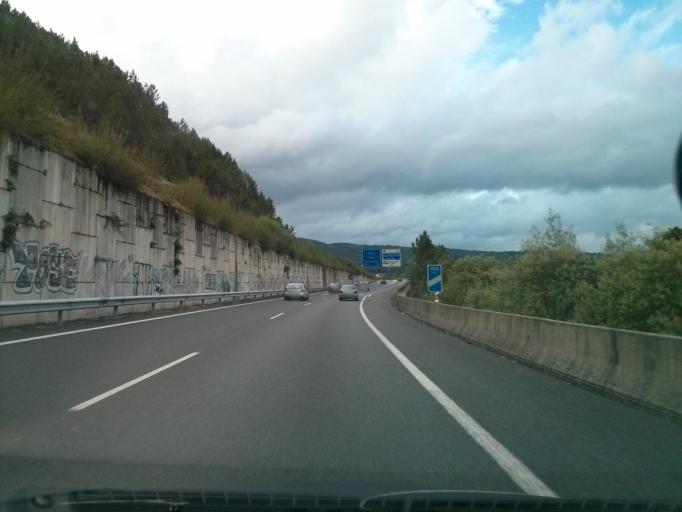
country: ES
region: Galicia
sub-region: Provincia de Ourense
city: Toen
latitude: 42.3367
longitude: -7.9863
